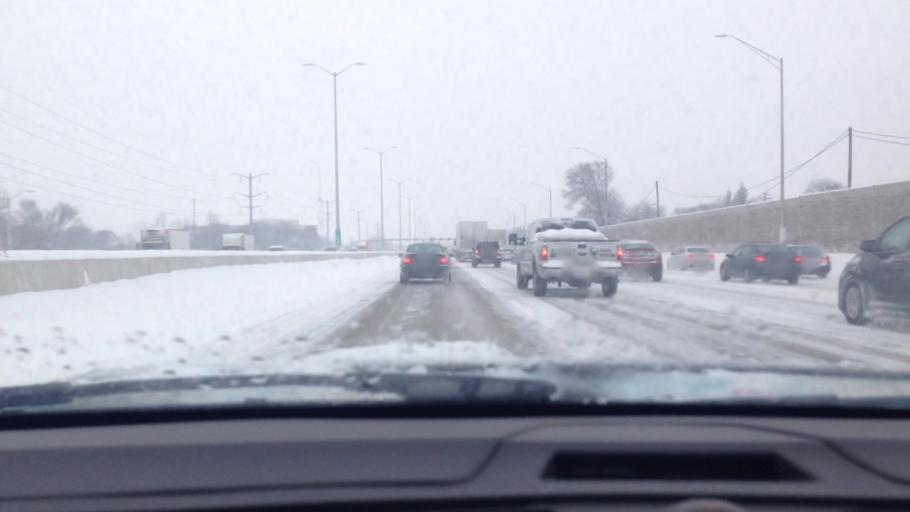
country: US
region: Illinois
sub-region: Cook County
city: Hoffman Estates
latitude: 42.0629
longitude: -88.0948
